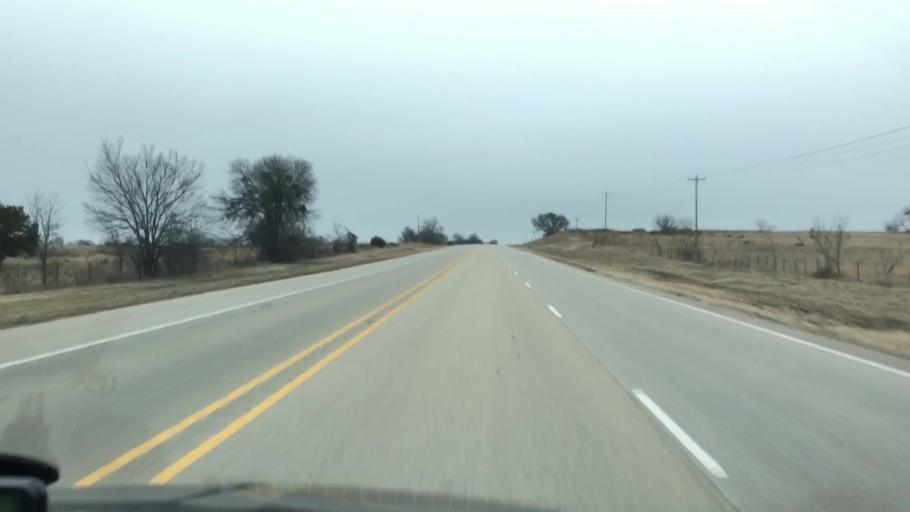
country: US
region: Texas
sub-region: Hamilton County
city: Hamilton
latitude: 31.6559
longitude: -98.1439
